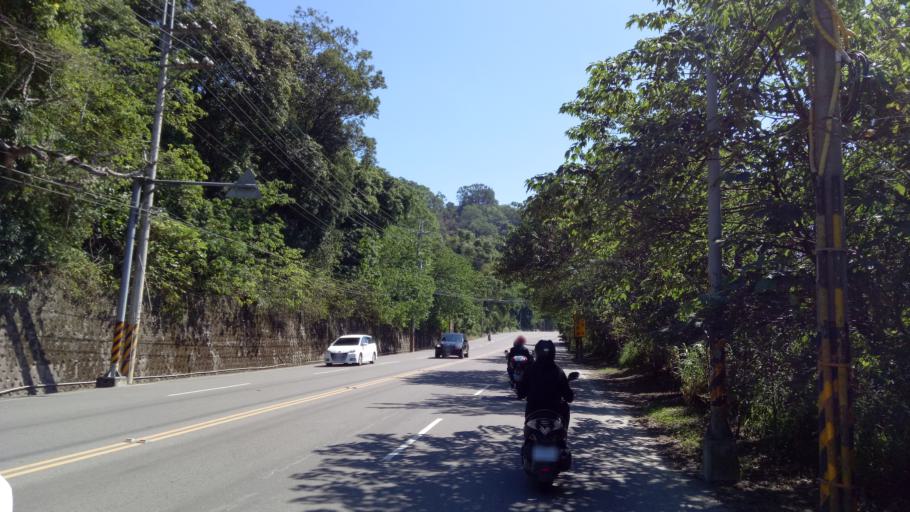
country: TW
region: Taiwan
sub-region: Hsinchu
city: Hsinchu
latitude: 24.6815
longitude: 120.9645
